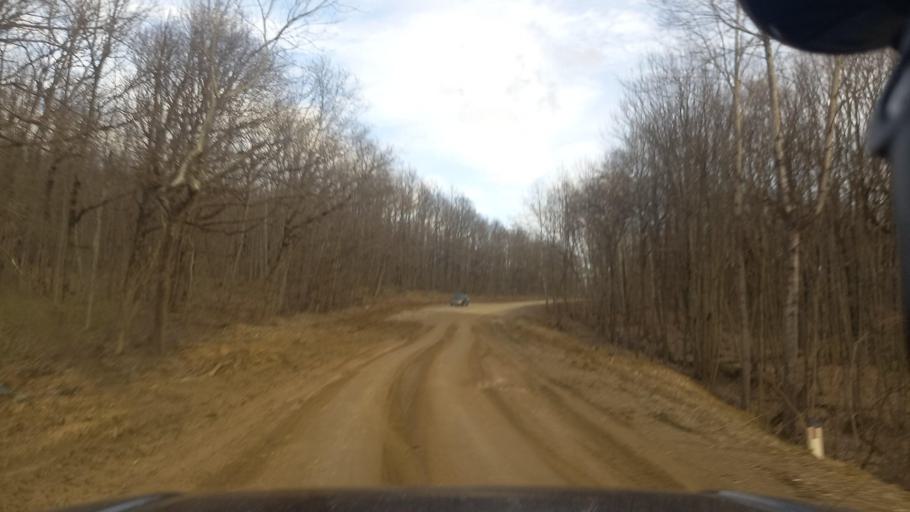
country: RU
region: Krasnodarskiy
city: Goryachiy Klyuch
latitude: 44.7004
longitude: 39.0188
